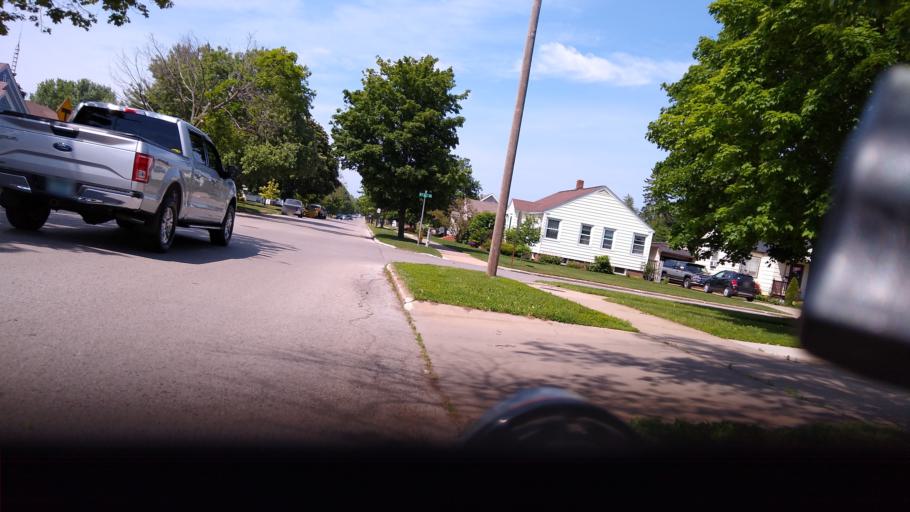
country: US
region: Michigan
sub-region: Delta County
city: Escanaba
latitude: 45.7359
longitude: -87.0739
